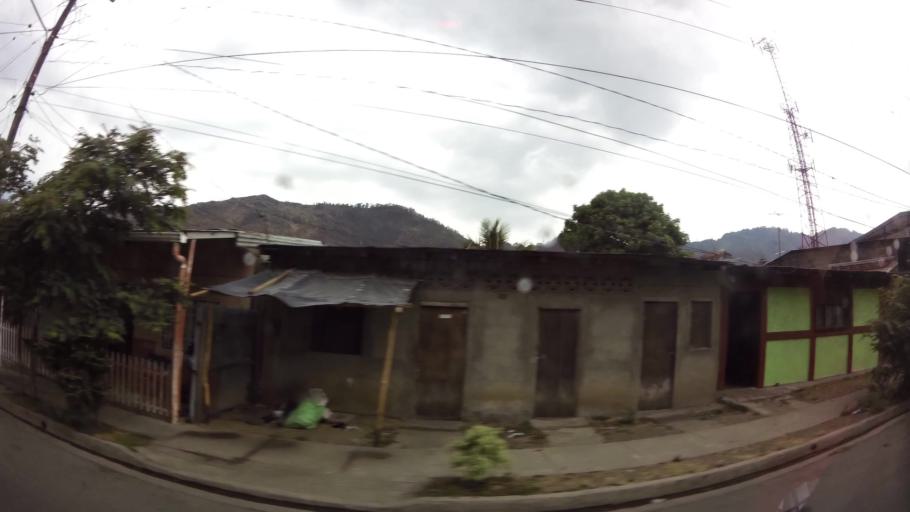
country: NI
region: Jinotega
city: Jinotega
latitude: 13.0920
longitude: -85.9982
